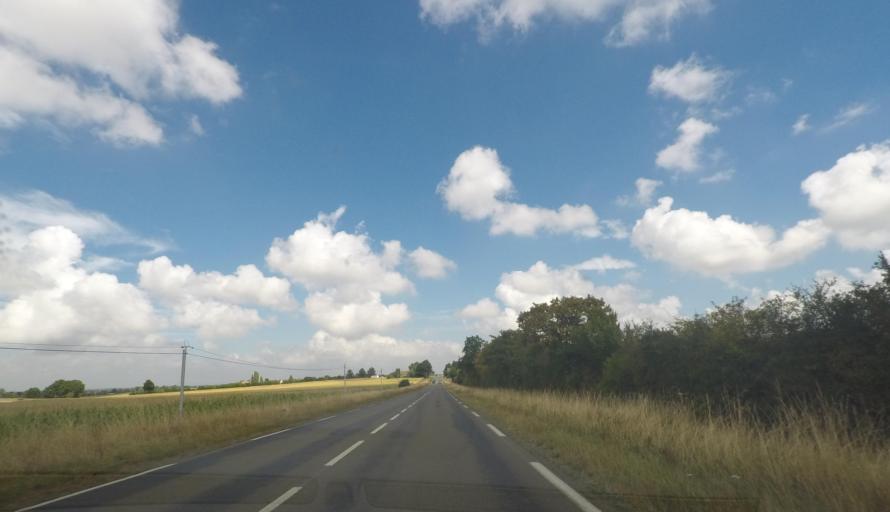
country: FR
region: Pays de la Loire
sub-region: Departement de la Sarthe
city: Saint-Cosme-en-Vairais
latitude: 48.2393
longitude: 0.4386
